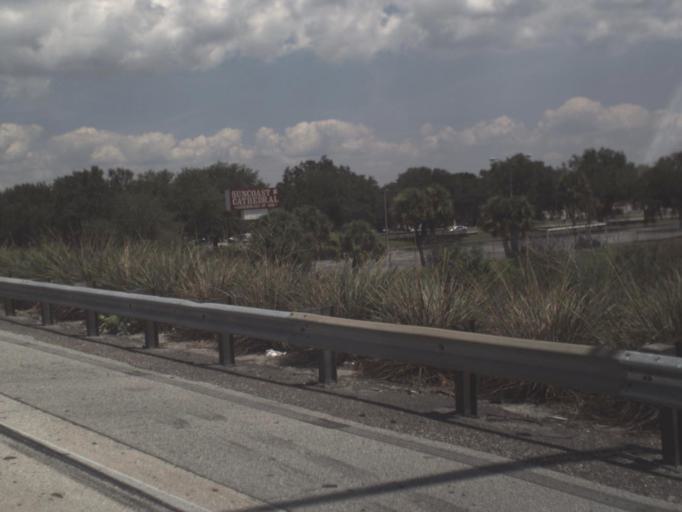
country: US
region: Florida
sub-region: Pinellas County
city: Lealman
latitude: 27.8267
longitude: -82.6661
